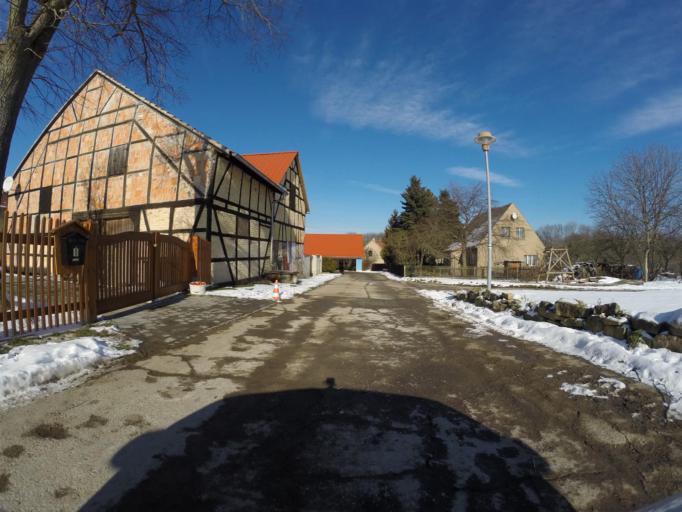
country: DE
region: Thuringia
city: Bucha
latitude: 50.8993
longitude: 11.5300
